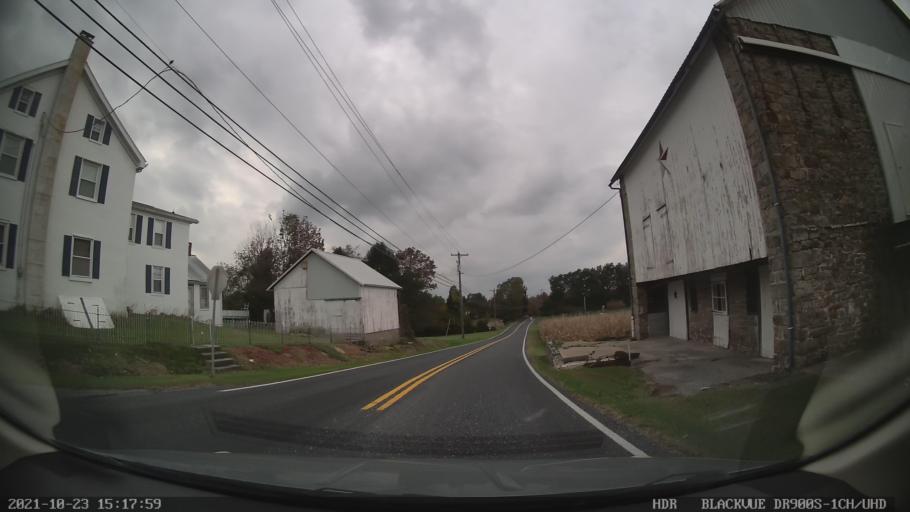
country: US
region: Pennsylvania
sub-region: Berks County
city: Topton
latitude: 40.4595
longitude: -75.7412
